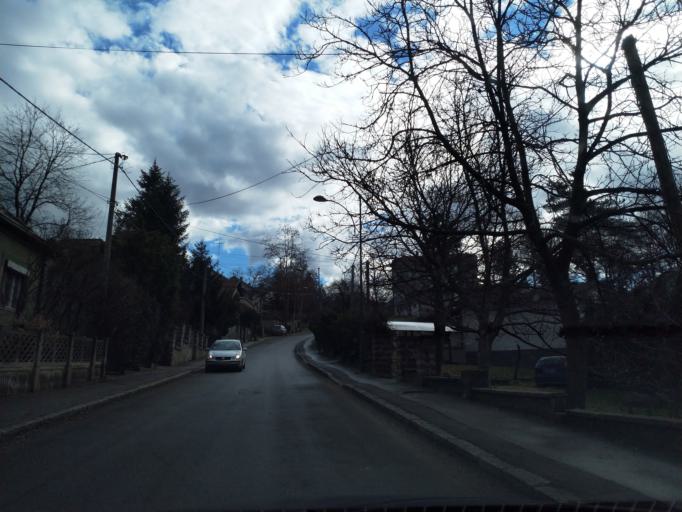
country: RS
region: Central Serbia
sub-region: Belgrade
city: Grocka
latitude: 44.6693
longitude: 20.7186
